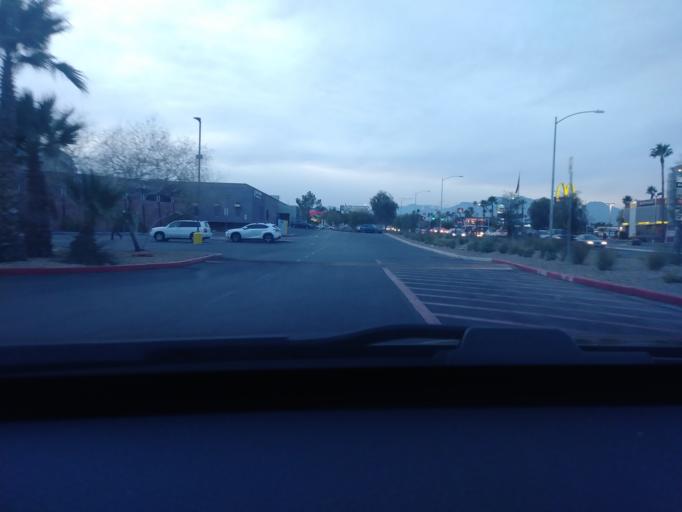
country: US
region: Nevada
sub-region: Clark County
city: Spring Valley
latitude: 36.1589
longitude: -115.2325
